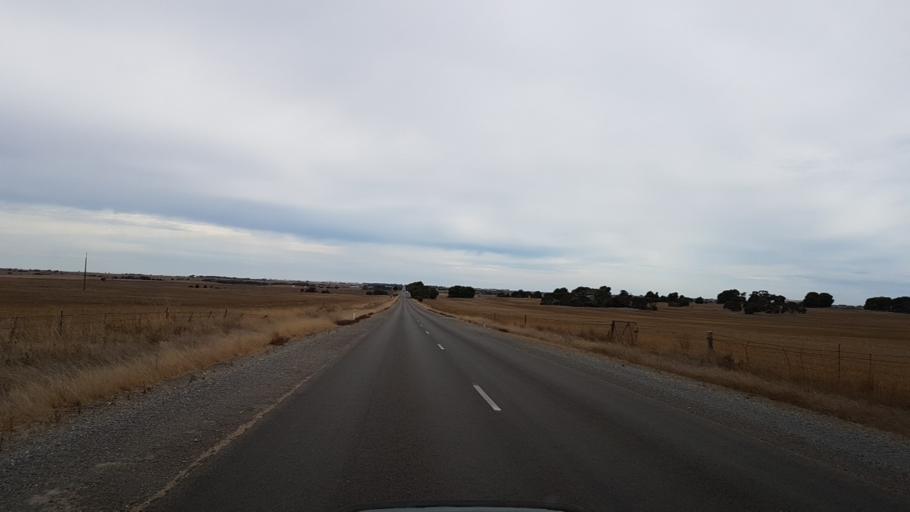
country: AU
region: South Australia
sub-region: Yorke Peninsula
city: Honiton
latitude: -34.9850
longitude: 137.3174
